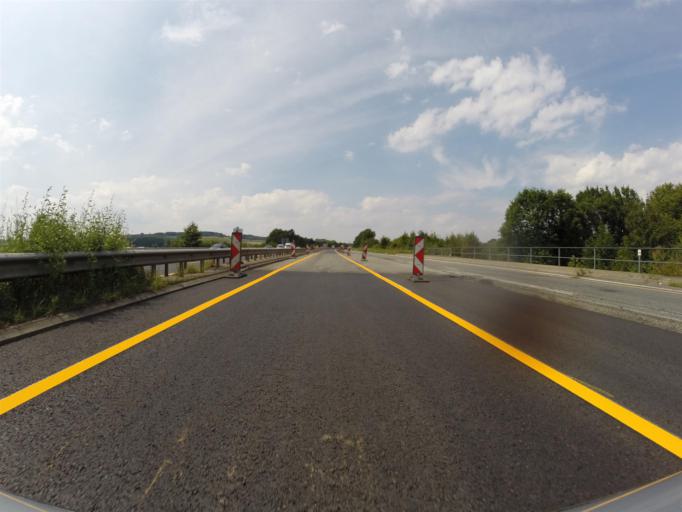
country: DE
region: North Rhine-Westphalia
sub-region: Regierungsbezirk Detmold
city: Kirchlengern
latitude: 52.1872
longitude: 8.6463
